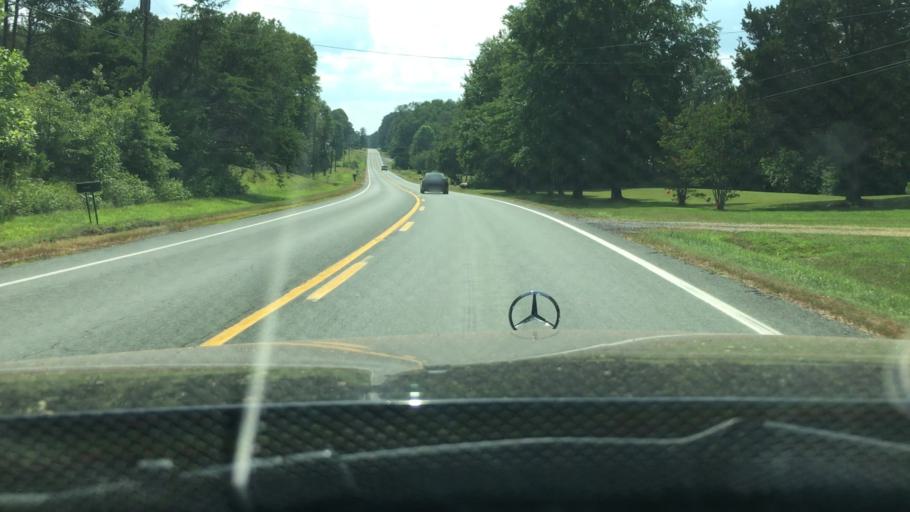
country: US
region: Virginia
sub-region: Orange County
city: Orange
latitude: 38.2584
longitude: -78.0059
